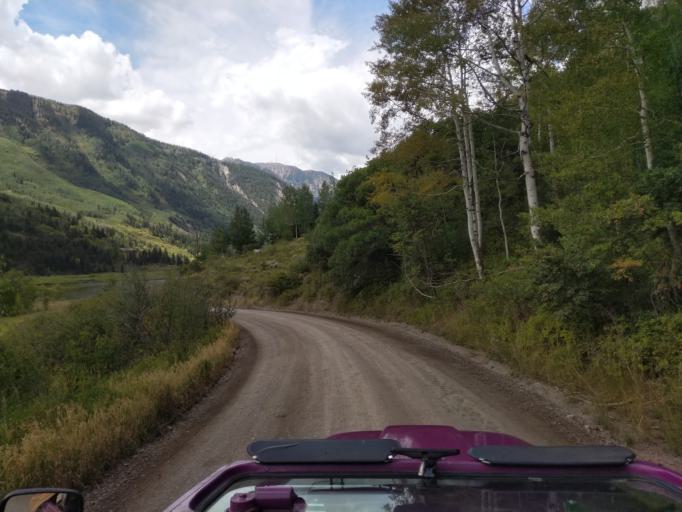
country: US
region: Colorado
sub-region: Gunnison County
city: Crested Butte
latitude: 39.0721
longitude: -107.1752
